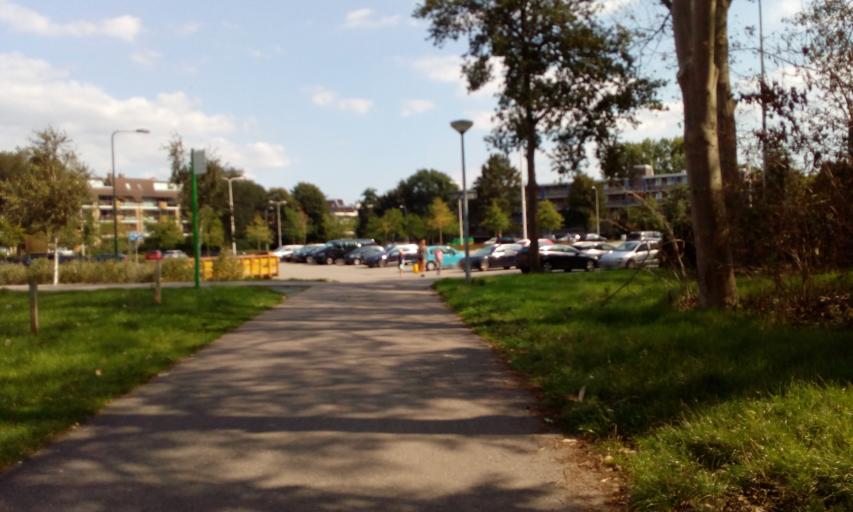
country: NL
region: South Holland
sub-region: Gemeente Gouda
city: Bloemendaal
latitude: 52.0234
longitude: 4.6890
